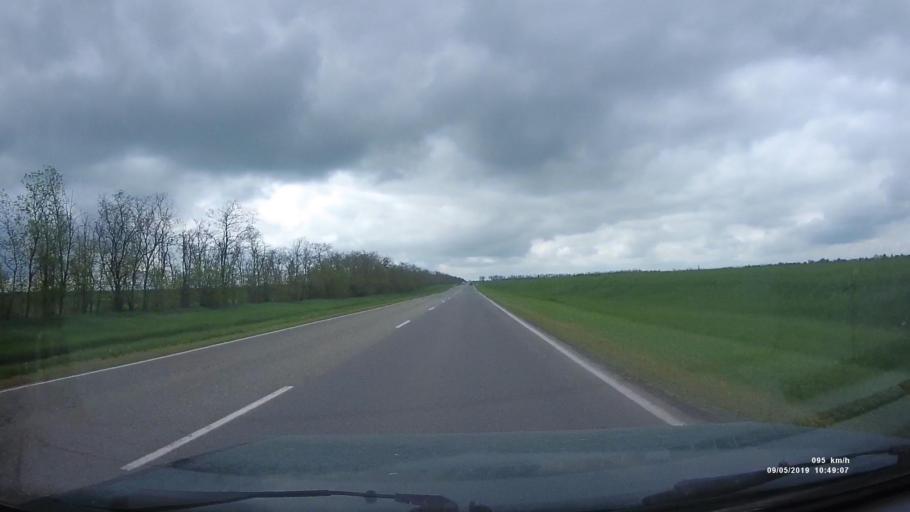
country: RU
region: Rostov
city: Peshkovo
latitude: 46.9471
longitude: 39.3560
